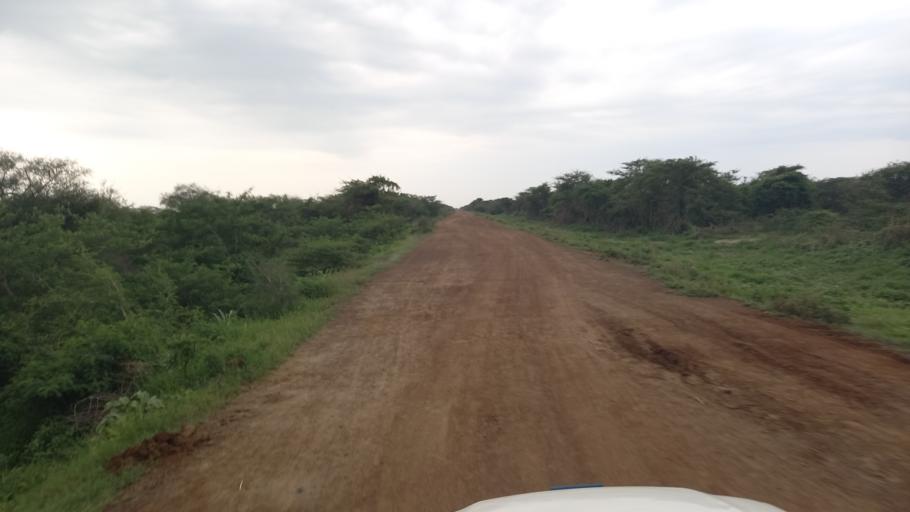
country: ET
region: Gambela
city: Gambela
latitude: 8.3430
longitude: 33.9122
